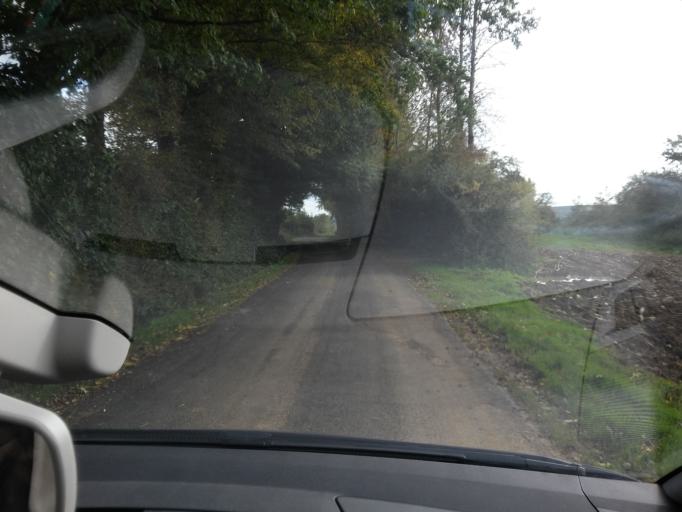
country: BE
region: Wallonia
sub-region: Province du Luxembourg
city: Arlon
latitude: 49.7057
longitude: 5.7892
